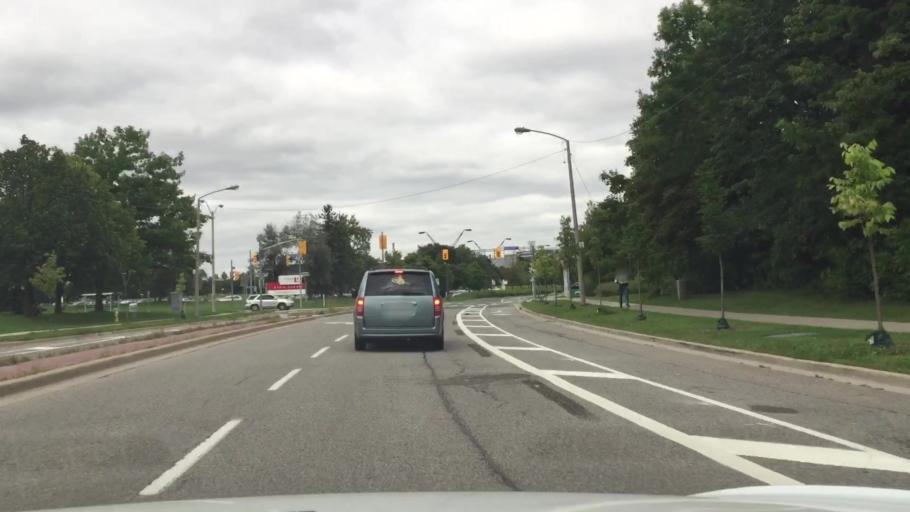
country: CA
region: Ontario
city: Concord
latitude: 43.7714
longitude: -79.5146
